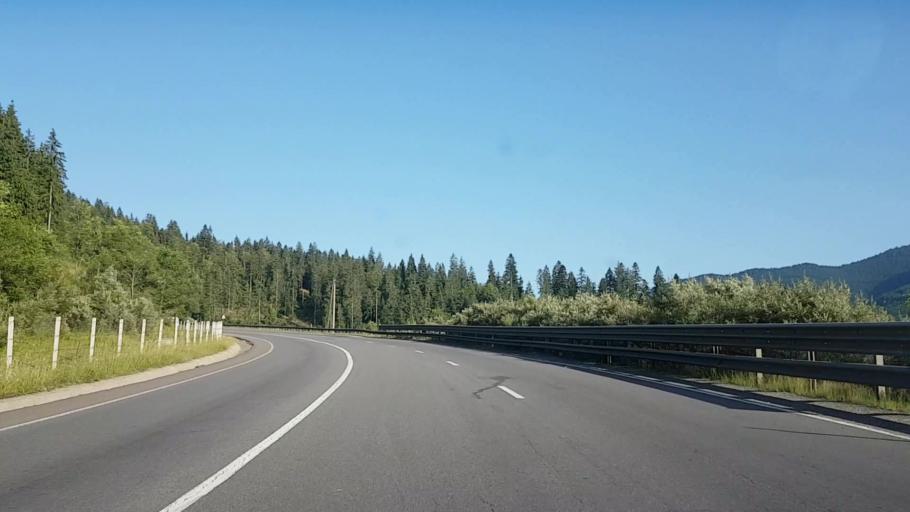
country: RO
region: Bistrita-Nasaud
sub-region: Comuna Lunca Ilvei
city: Lunca Ilvei
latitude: 47.2285
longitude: 24.9676
